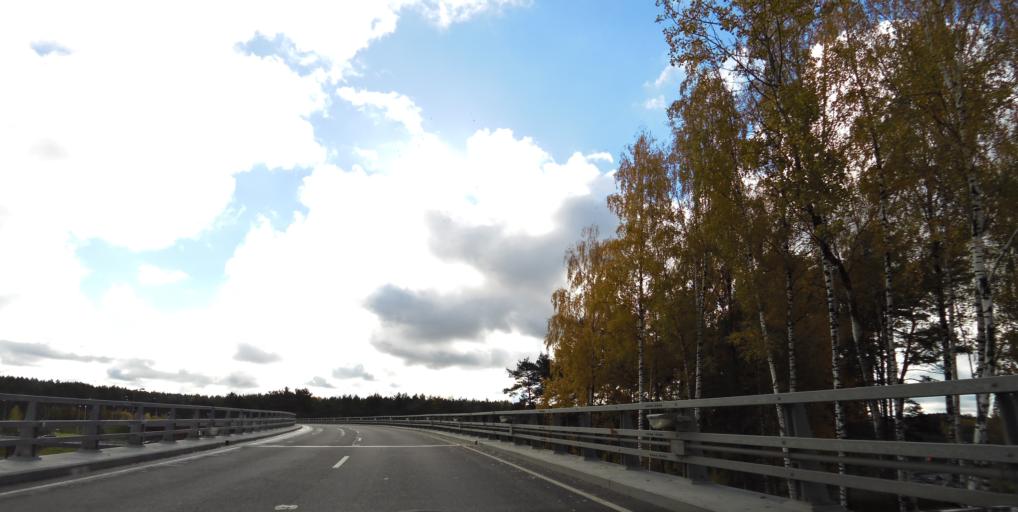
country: LT
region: Vilnius County
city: Lazdynai
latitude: 54.6731
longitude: 25.1957
